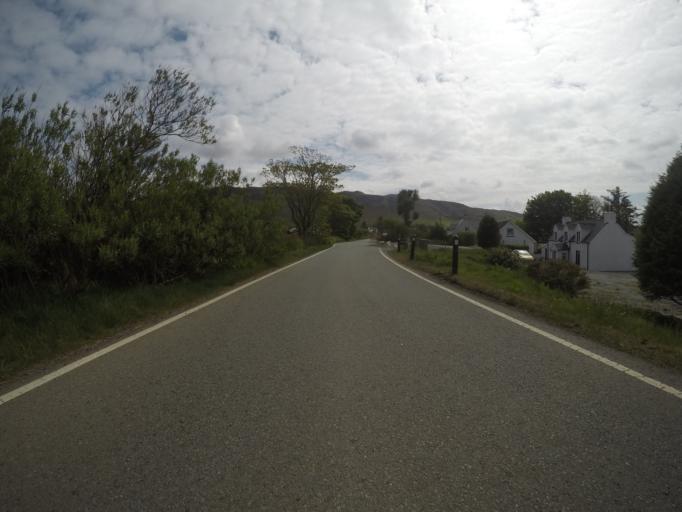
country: GB
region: Scotland
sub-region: Highland
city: Portree
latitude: 57.6213
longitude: -6.3747
